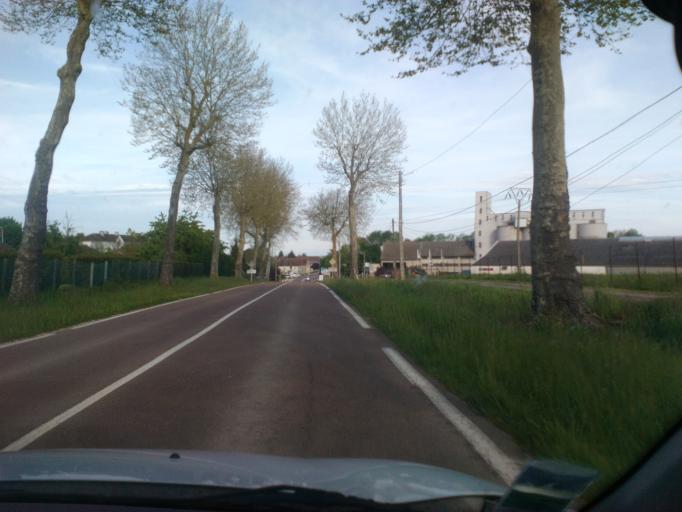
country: FR
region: Champagne-Ardenne
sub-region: Departement de l'Aube
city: Vendeuvre-sur-Barse
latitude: 48.2392
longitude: 4.4787
